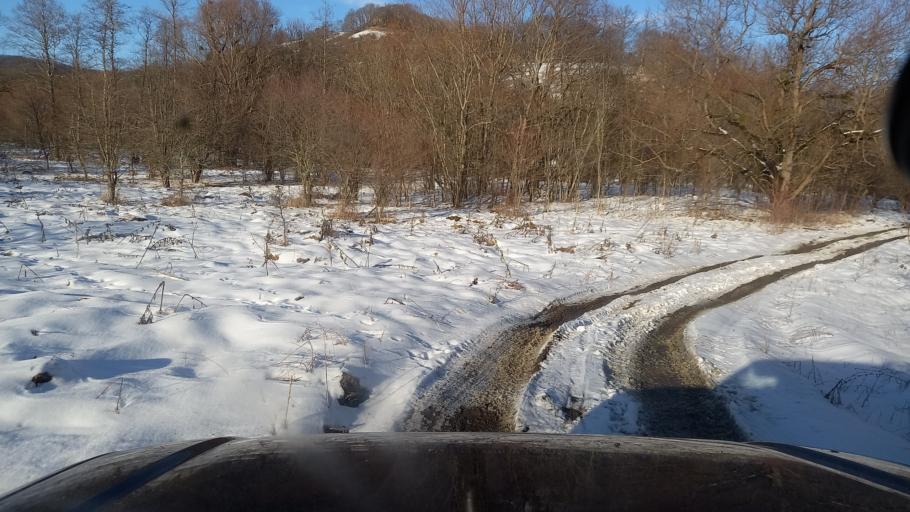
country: RU
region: Adygeya
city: Kamennomostskiy
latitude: 44.2032
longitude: 40.1502
